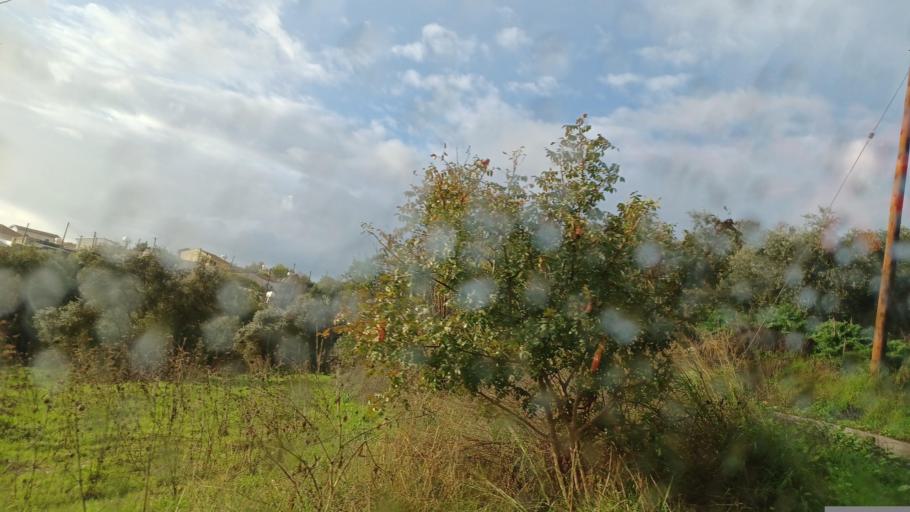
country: CY
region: Pafos
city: Mesogi
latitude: 34.8598
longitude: 32.5099
